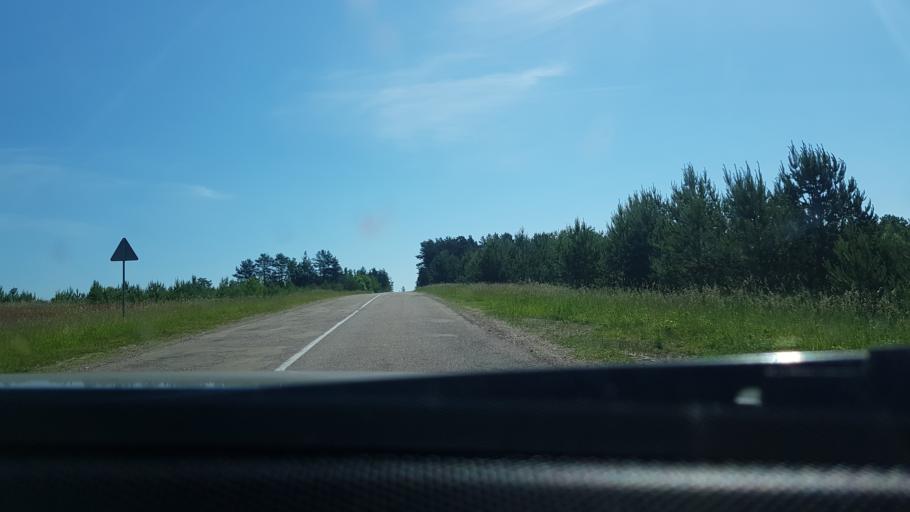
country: LV
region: Kraslavas Rajons
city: Kraslava
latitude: 55.8628
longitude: 26.9801
